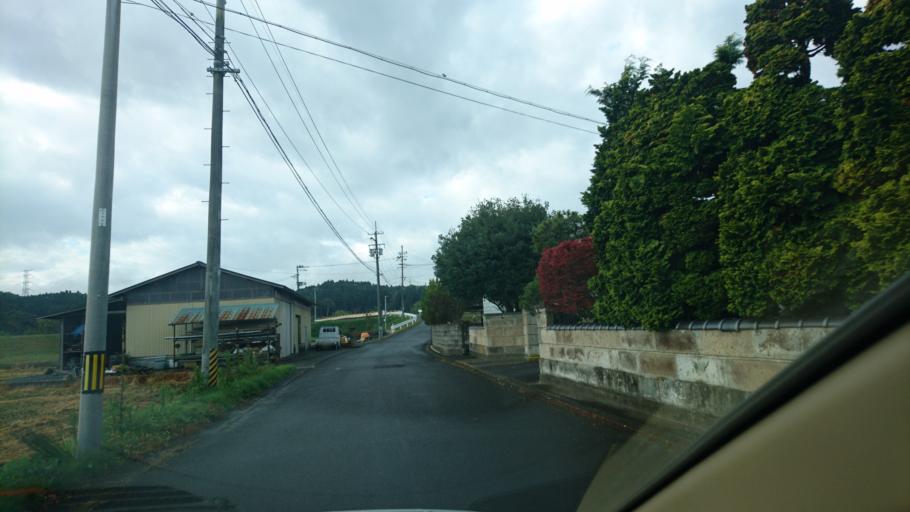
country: JP
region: Iwate
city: Ichinoseki
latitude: 38.7990
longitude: 140.9907
